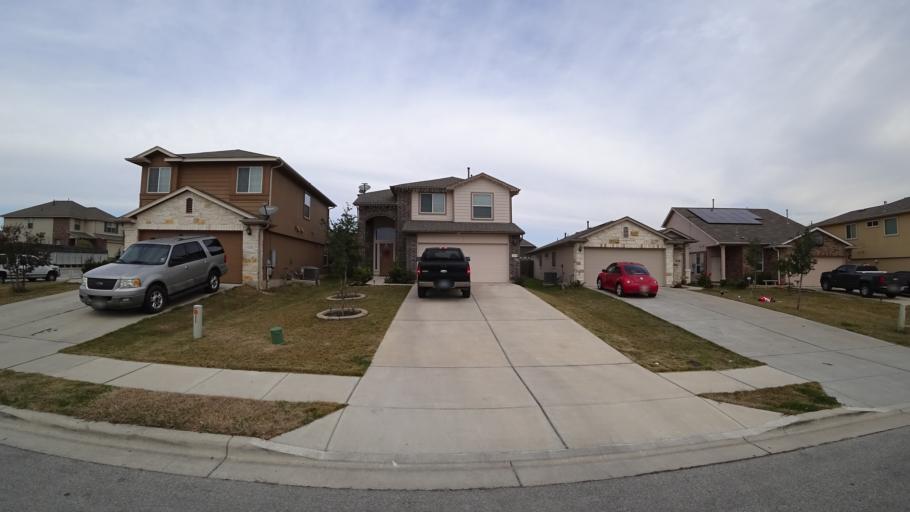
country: US
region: Texas
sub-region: Travis County
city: Garfield
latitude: 30.1591
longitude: -97.6371
